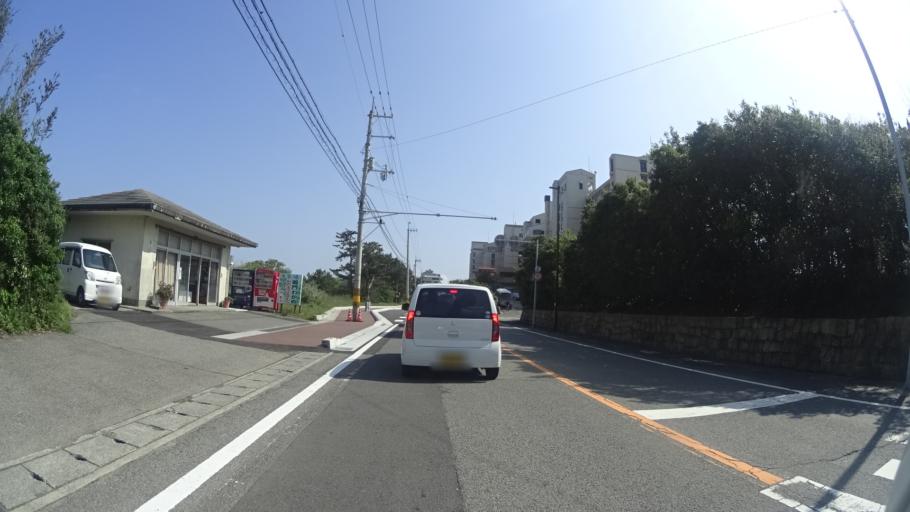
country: JP
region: Tokushima
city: Narutocho-mitsuishi
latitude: 34.2191
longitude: 134.6317
